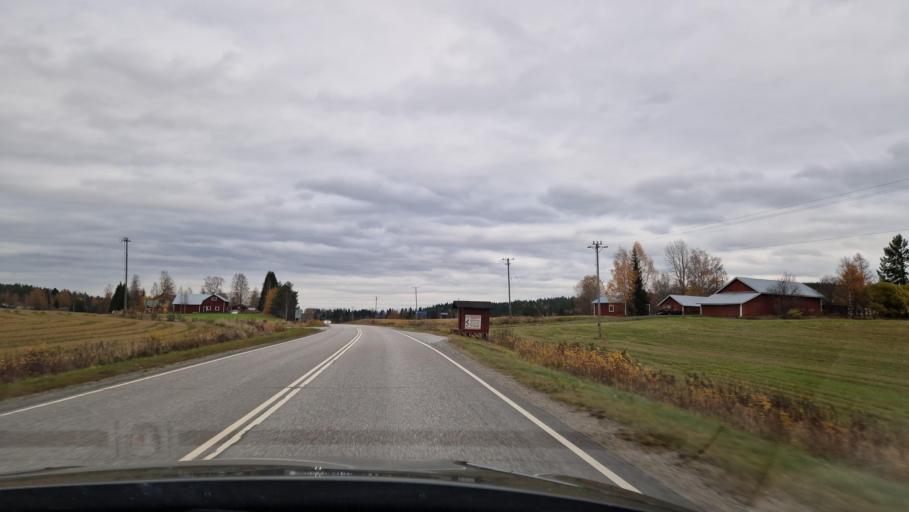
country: FI
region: North Karelia
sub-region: Pielisen Karjala
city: Valtimo
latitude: 63.5218
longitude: 28.8875
